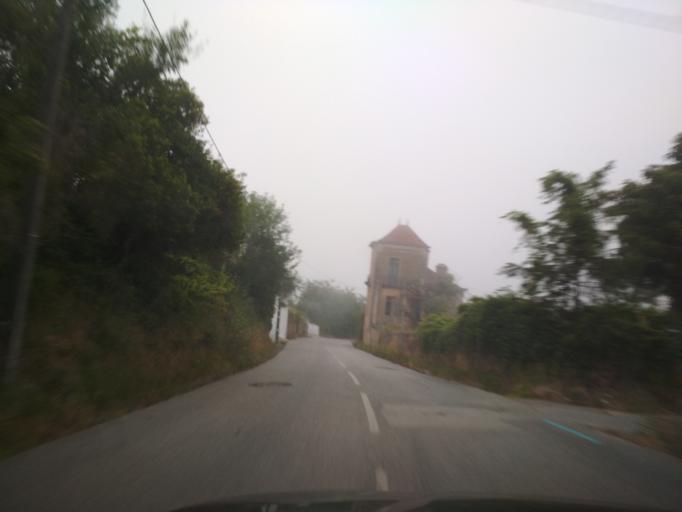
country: PT
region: Coimbra
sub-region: Coimbra
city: Coimbra
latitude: 40.1806
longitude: -8.4491
